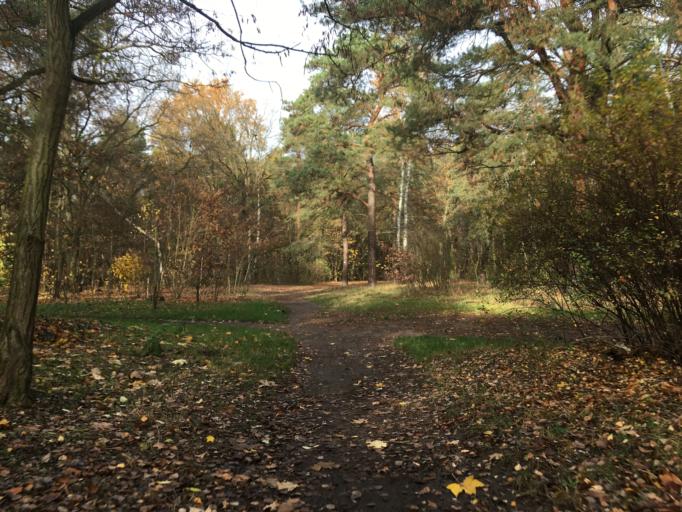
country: DE
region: Berlin
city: Adlershof
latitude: 52.4429
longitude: 13.5417
